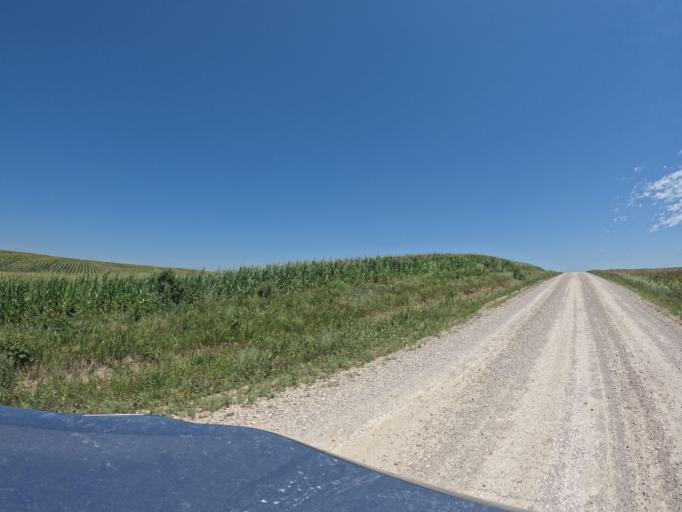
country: US
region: Iowa
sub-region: Keokuk County
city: Sigourney
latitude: 41.4523
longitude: -92.3637
